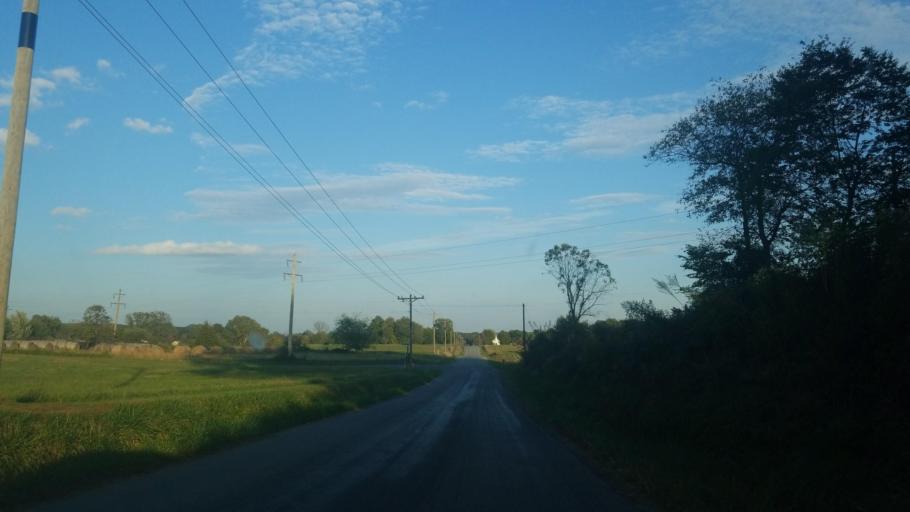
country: US
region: Illinois
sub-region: Saline County
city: Harrisburg
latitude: 37.8048
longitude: -88.6156
